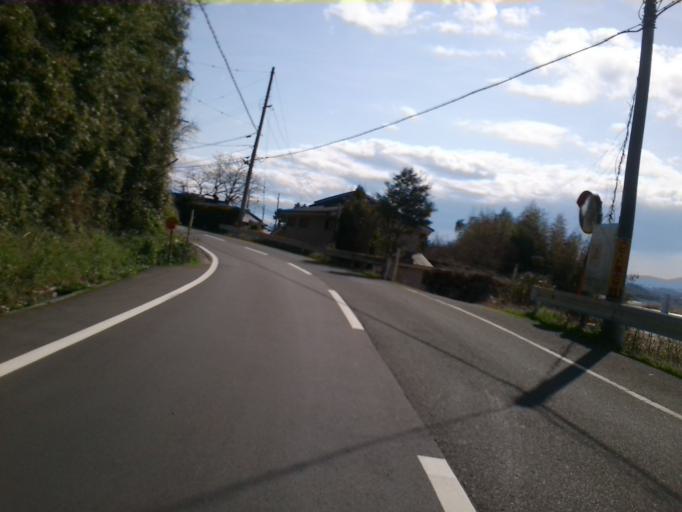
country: JP
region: Nara
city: Nara-shi
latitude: 34.7500
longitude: 135.8366
